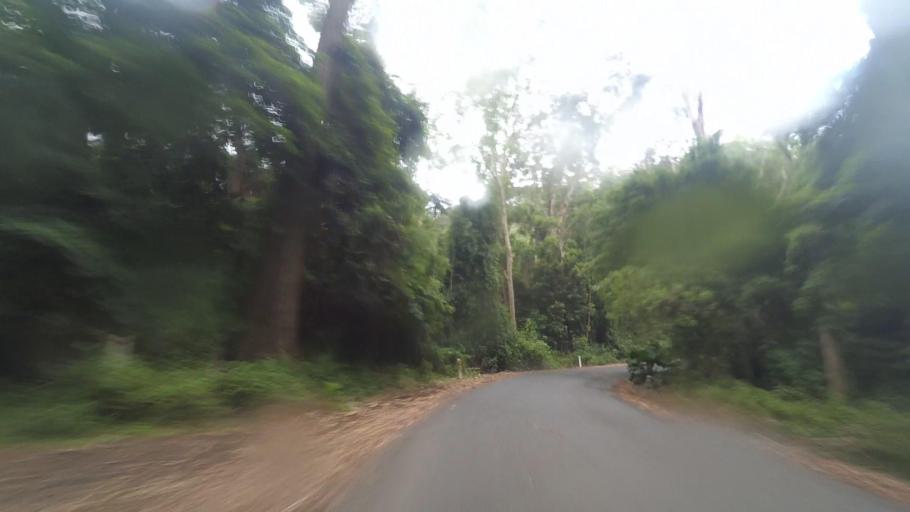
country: AU
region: New South Wales
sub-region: Wollongong
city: Mount Keira
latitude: -34.4025
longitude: 150.8252
